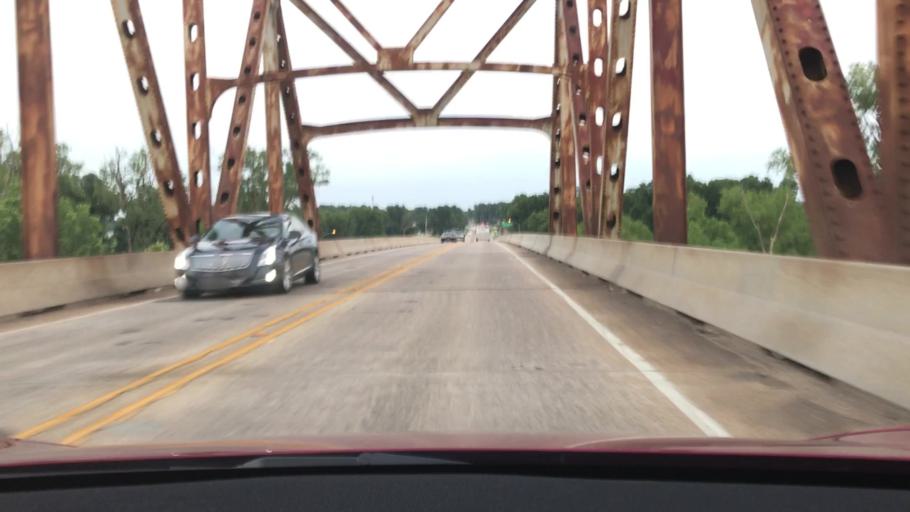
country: US
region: Louisiana
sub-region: Bossier Parish
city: Bossier City
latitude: 32.4589
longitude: -93.6771
